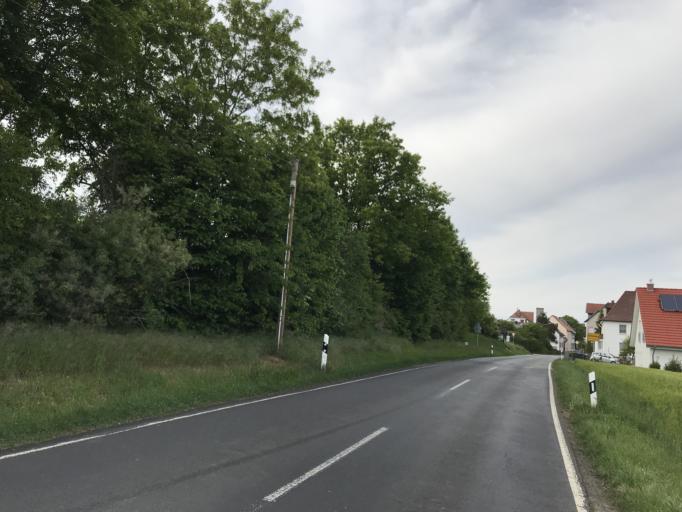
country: DE
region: Hesse
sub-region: Regierungsbezirk Giessen
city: Hoernsheim
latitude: 50.5077
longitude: 8.6146
